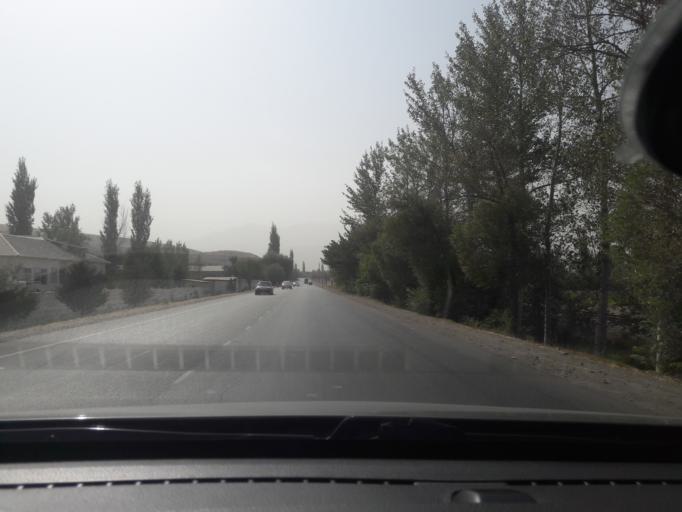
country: TJ
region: Republican Subordination
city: Vahdat
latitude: 38.5254
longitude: 69.0274
